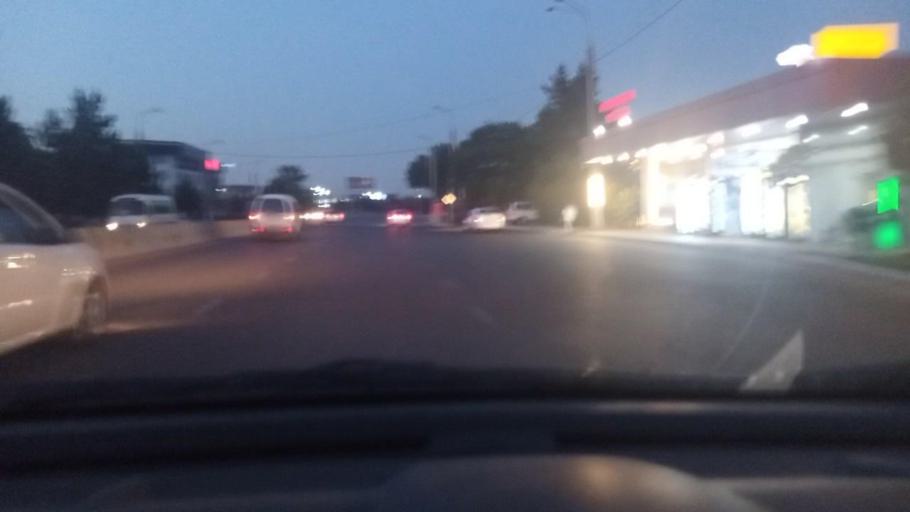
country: UZ
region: Toshkent Shahri
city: Tashkent
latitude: 41.2482
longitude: 69.2180
